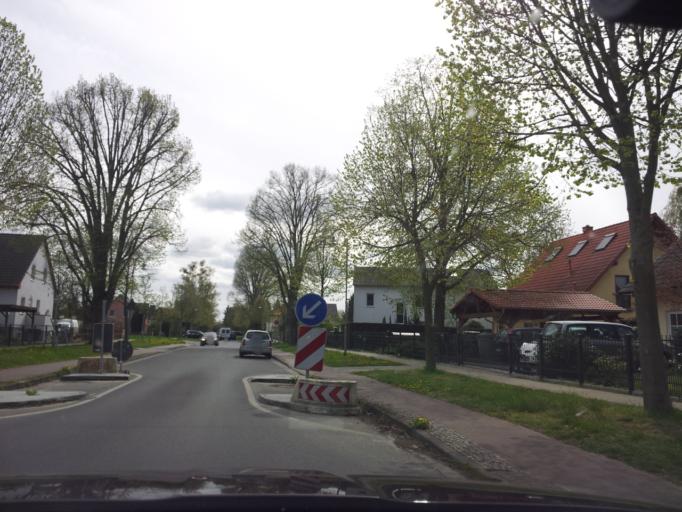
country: DE
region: Brandenburg
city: Teltow
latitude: 52.3907
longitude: 13.2829
